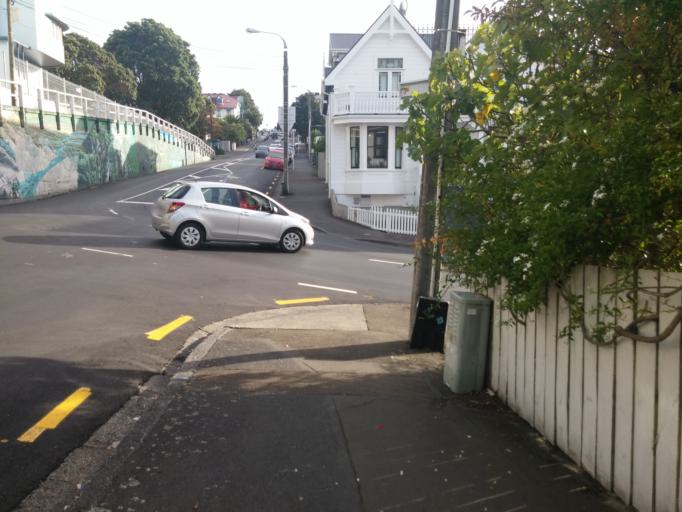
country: NZ
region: Wellington
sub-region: Wellington City
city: Wellington
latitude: -41.2918
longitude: 174.7706
